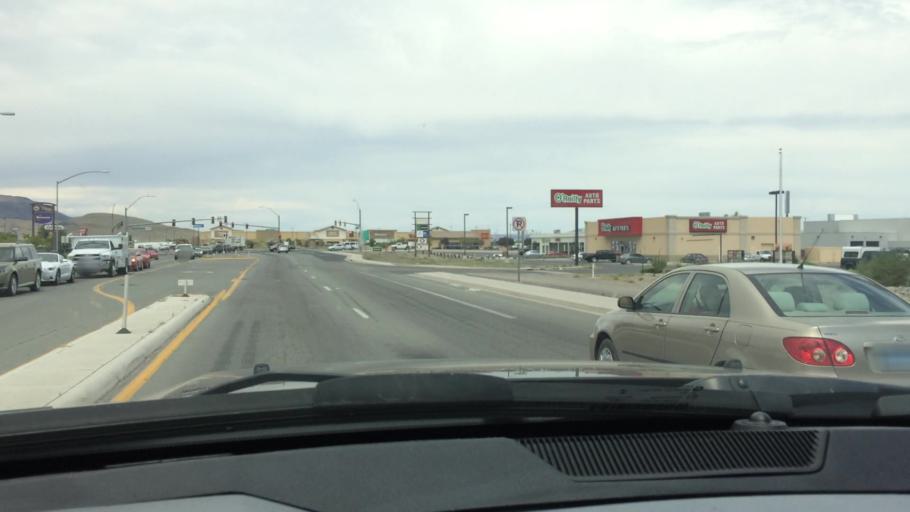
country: US
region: Nevada
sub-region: Lyon County
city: Fernley
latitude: 39.6082
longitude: -119.2216
